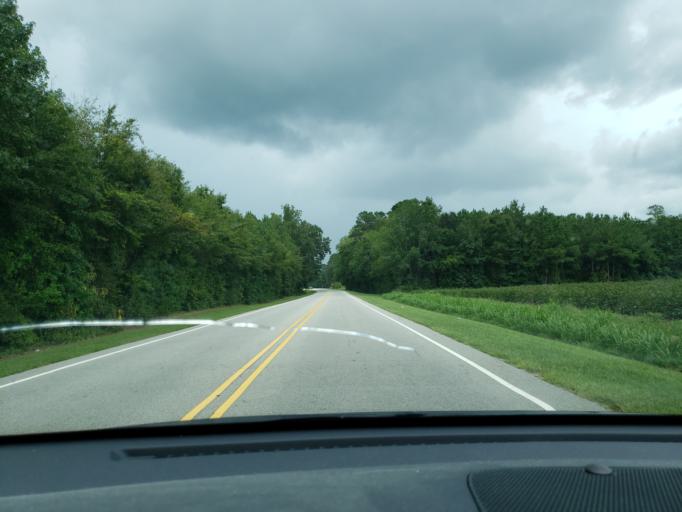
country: US
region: North Carolina
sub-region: Bladen County
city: Bladenboro
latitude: 34.4985
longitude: -78.6571
